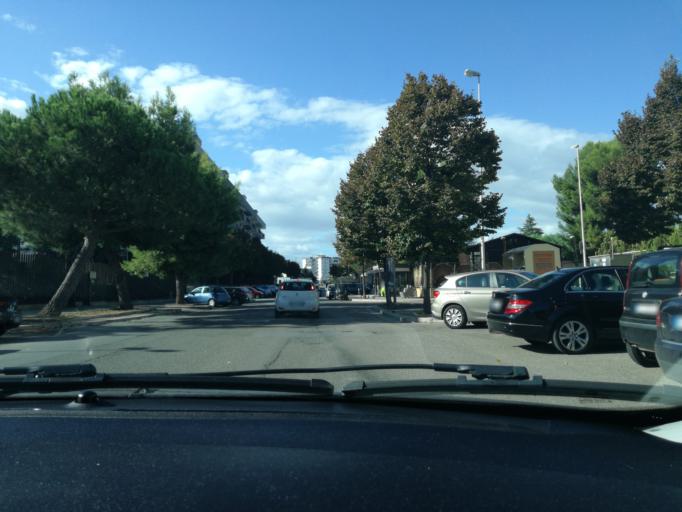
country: IT
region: Apulia
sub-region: Provincia di Bari
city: Triggiano
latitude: 41.0714
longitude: 16.9311
